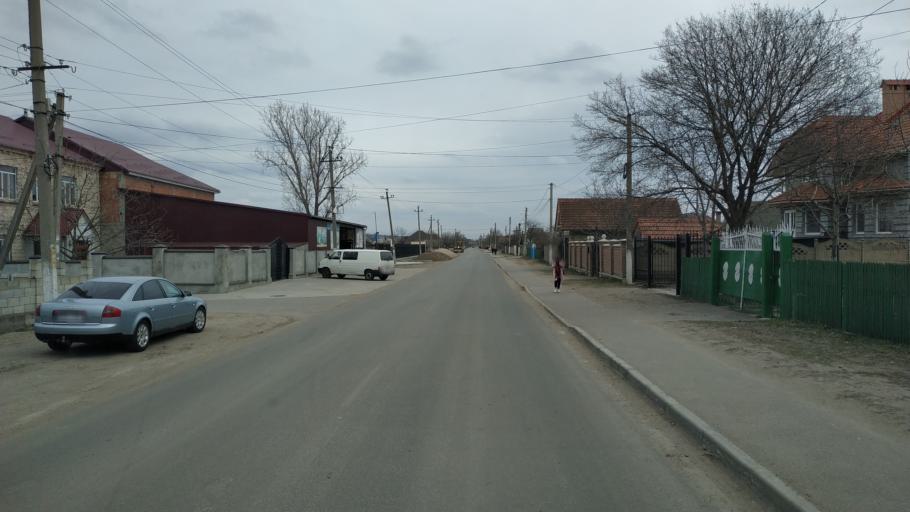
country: MD
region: Laloveni
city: Ialoveni
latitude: 46.8660
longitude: 28.7722
